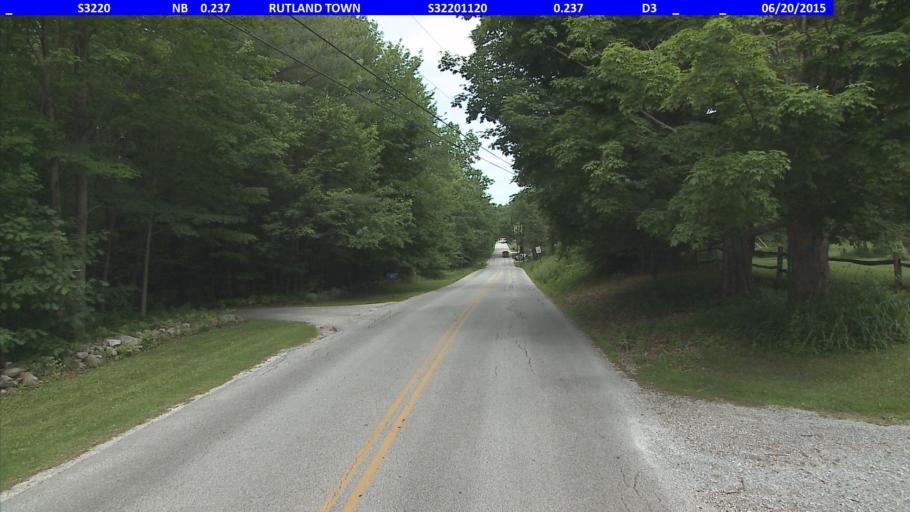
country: US
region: Vermont
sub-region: Rutland County
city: Rutland
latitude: 43.6122
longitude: -72.9362
